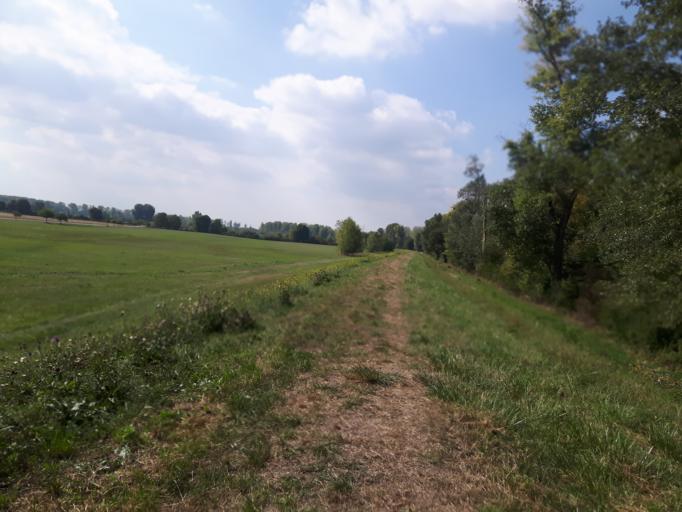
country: DE
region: Rheinland-Pfalz
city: Otterstadt
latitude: 49.3906
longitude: 8.4762
